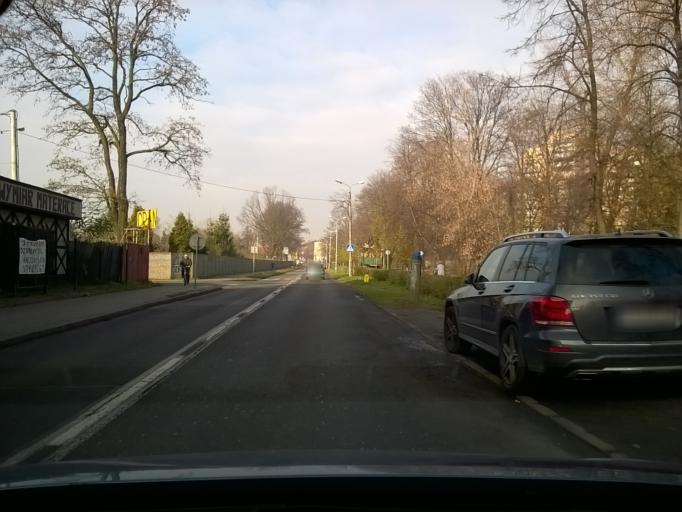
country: PL
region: Silesian Voivodeship
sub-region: Chorzow
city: Chorzow
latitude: 50.2834
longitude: 18.9525
